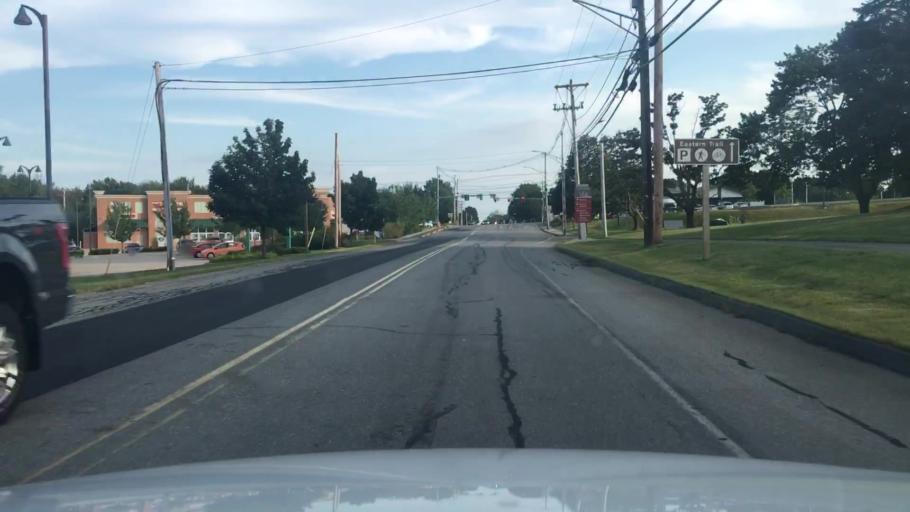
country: US
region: Maine
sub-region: Cumberland County
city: Scarborough
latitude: 43.5921
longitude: -70.3348
